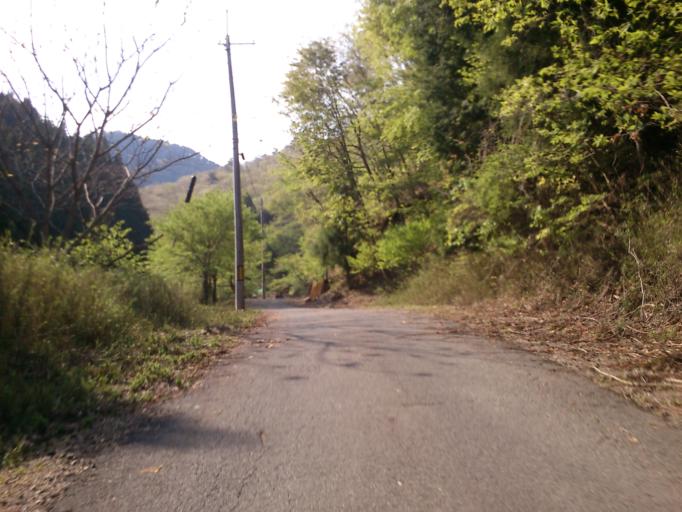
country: JP
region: Kyoto
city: Fukuchiyama
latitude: 35.3824
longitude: 135.0058
